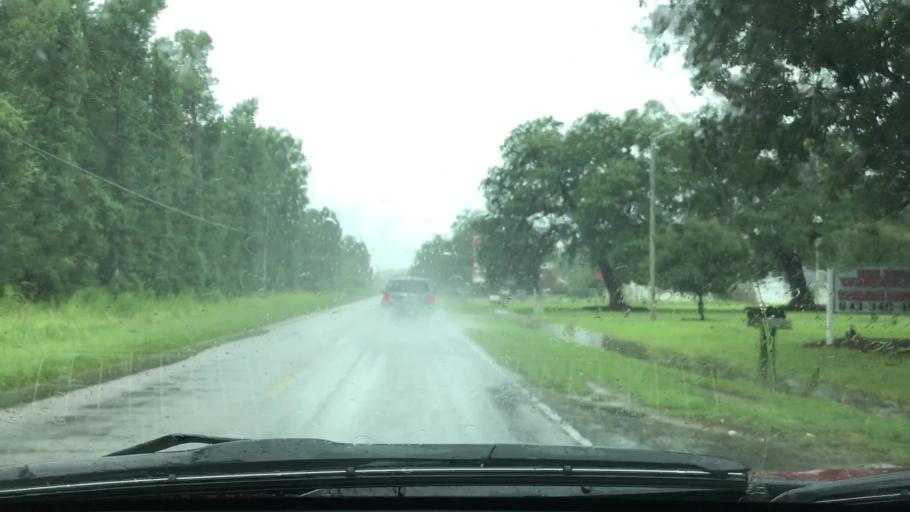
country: US
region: South Carolina
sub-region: Horry County
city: Red Hill
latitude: 33.8679
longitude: -78.9858
